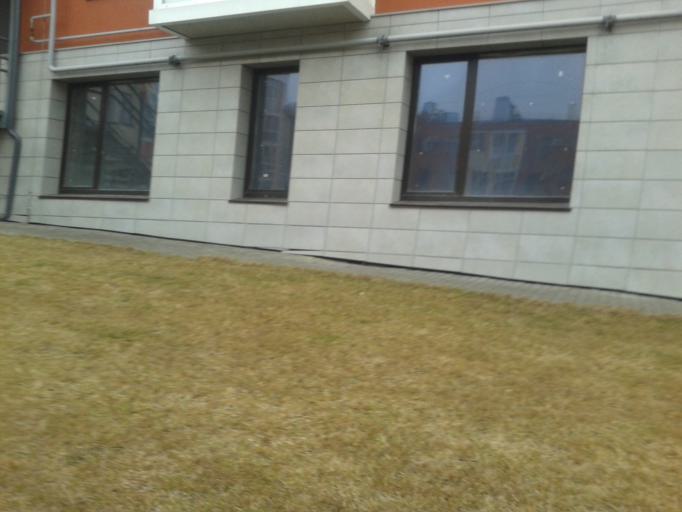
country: RU
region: Volgograd
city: Volgograd
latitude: 48.6629
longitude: 44.4138
